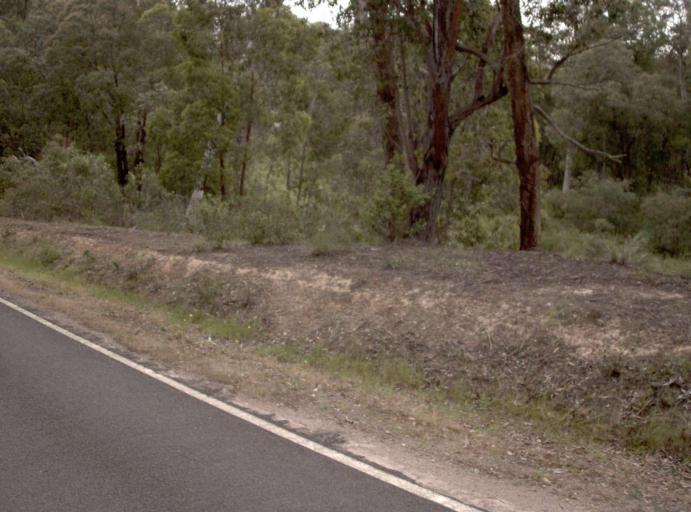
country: AU
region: Victoria
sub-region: East Gippsland
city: Bairnsdale
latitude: -37.6413
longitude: 147.2614
